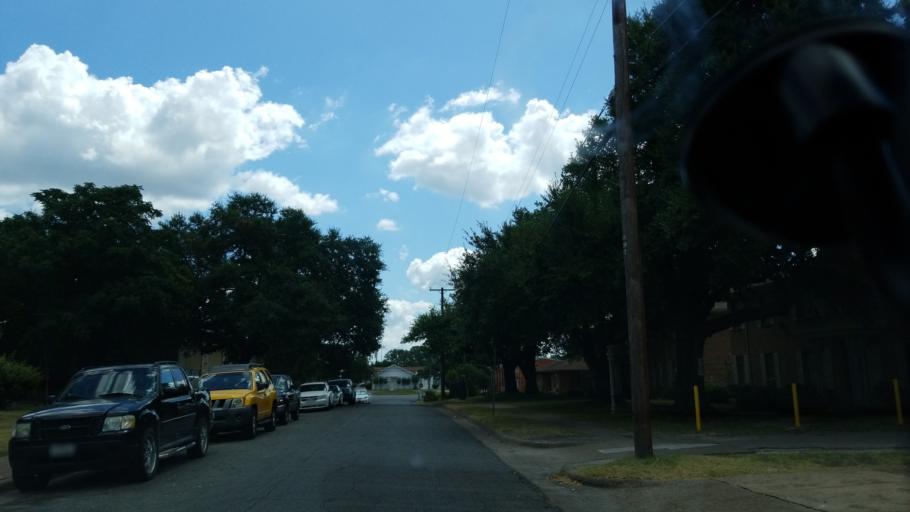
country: US
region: Texas
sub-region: Dallas County
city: Cockrell Hill
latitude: 32.7038
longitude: -96.8416
